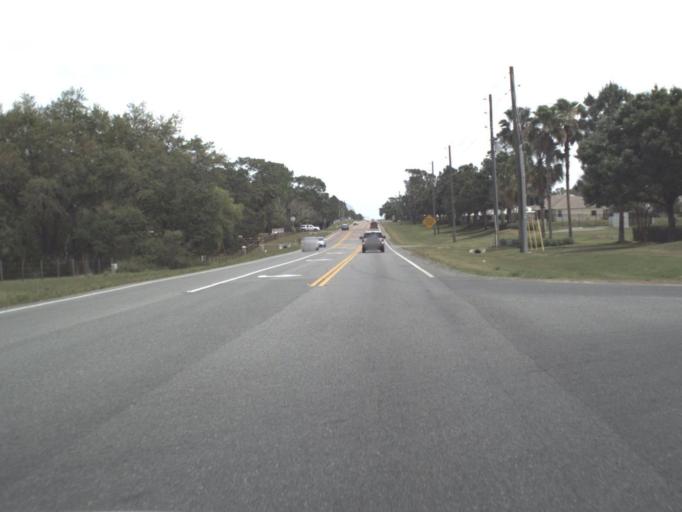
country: US
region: Florida
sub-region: Lake County
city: Mount Dora
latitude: 28.8517
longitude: -81.6205
